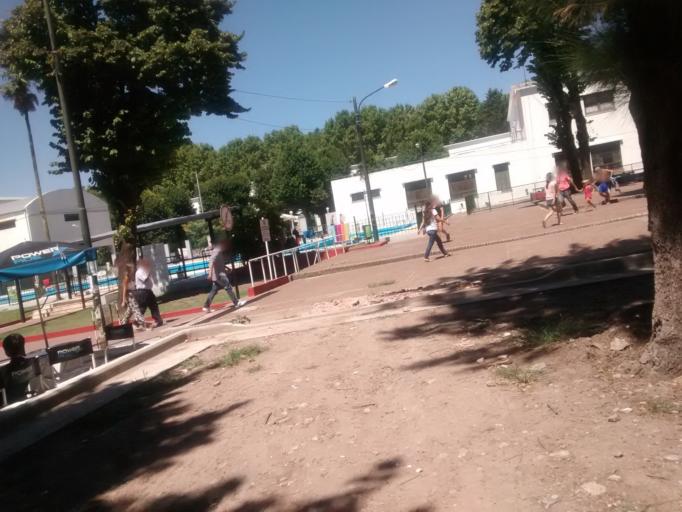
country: AR
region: Buenos Aires
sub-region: Partido de La Plata
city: La Plata
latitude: -34.9053
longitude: -57.9412
